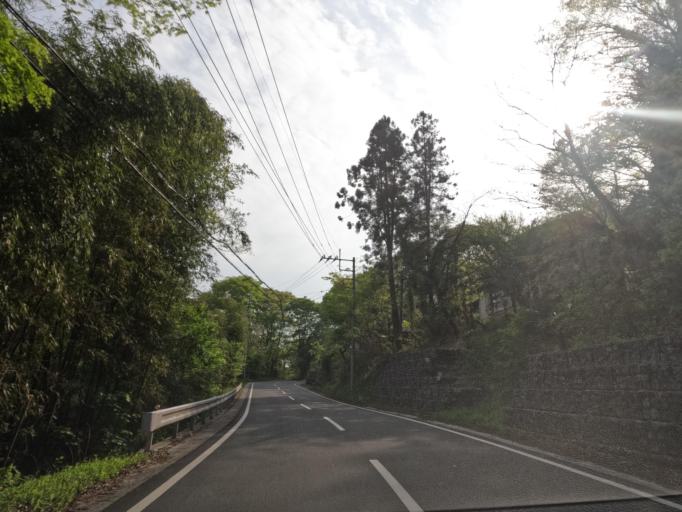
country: JP
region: Saitama
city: Chichibu
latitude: 36.0832
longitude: 139.1001
